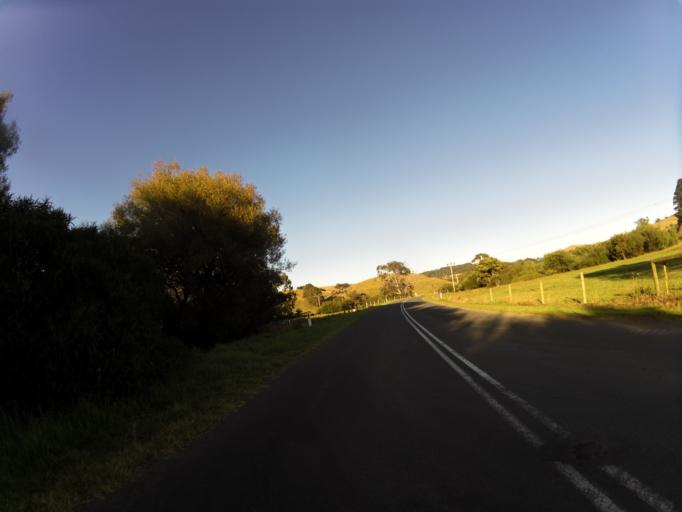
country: AU
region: Victoria
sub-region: Colac-Otway
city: Apollo Bay
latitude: -38.7694
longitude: 143.6490
